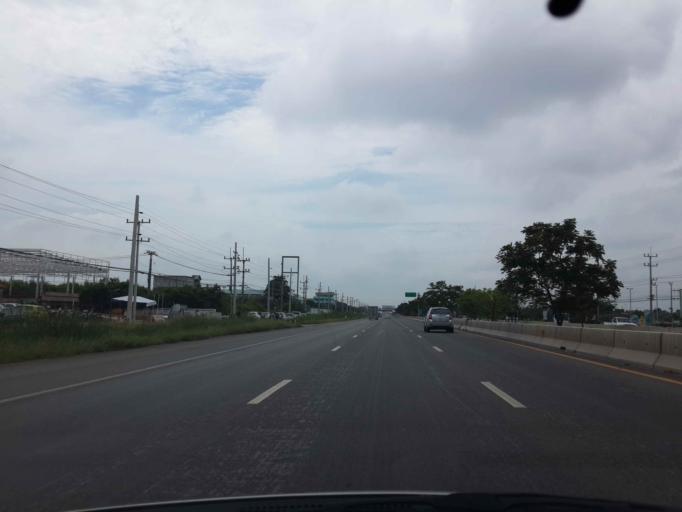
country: TH
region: Samut Songkhram
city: Samut Songkhram
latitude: 13.4332
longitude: 100.0523
